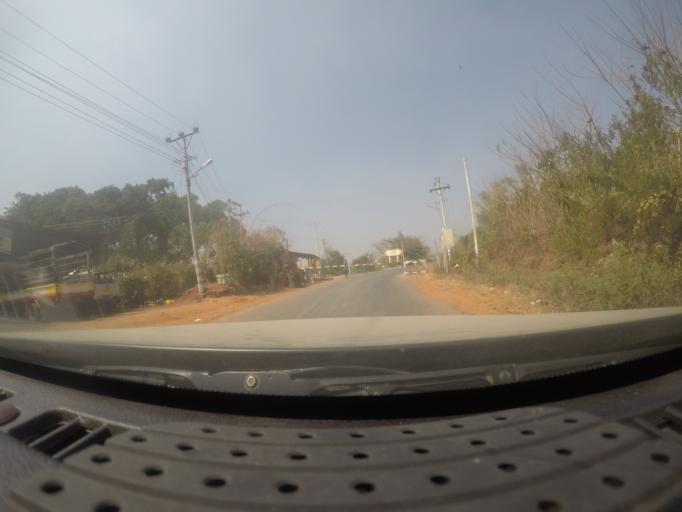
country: MM
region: Mandalay
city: Kyaukse
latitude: 21.1508
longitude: 96.4429
